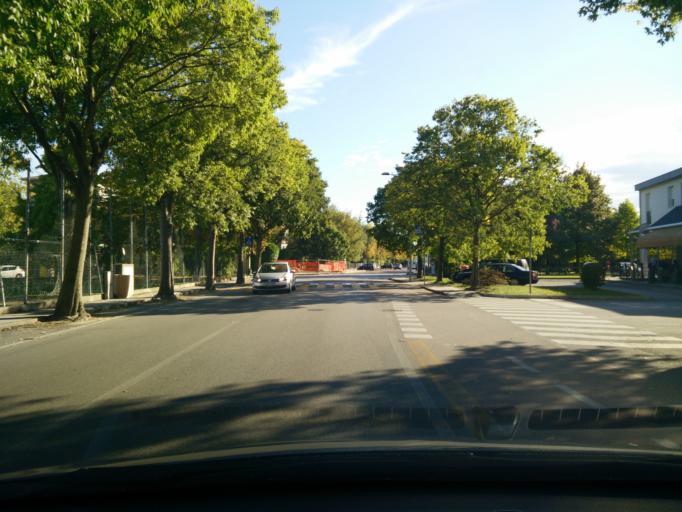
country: IT
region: Veneto
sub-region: Provincia di Venezia
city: San Dona di Piave
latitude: 45.6291
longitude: 12.5908
